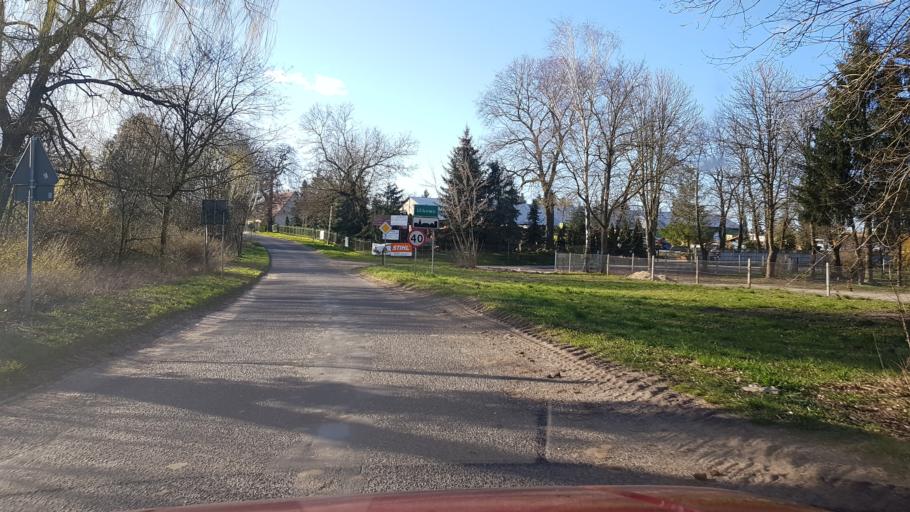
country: PL
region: West Pomeranian Voivodeship
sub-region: Powiat stargardzki
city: Stara Dabrowa
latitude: 53.3484
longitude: 15.1454
